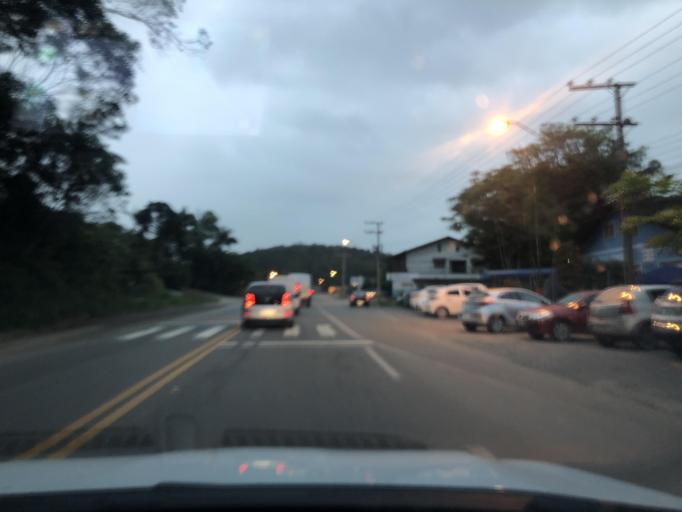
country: BR
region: Santa Catarina
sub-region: Pomerode
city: Pomerode
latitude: -26.7948
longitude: -49.0868
